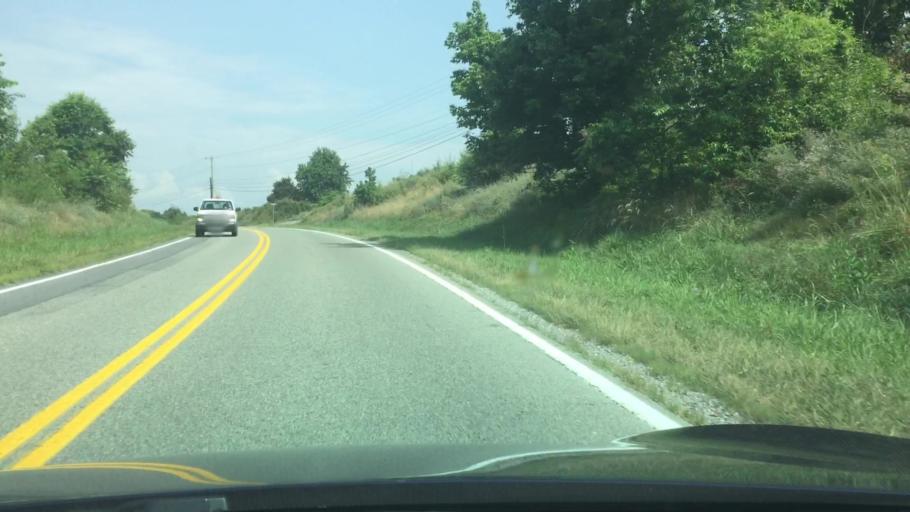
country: US
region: Virginia
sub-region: Wythe County
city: Wytheville
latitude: 36.9506
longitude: -80.9222
